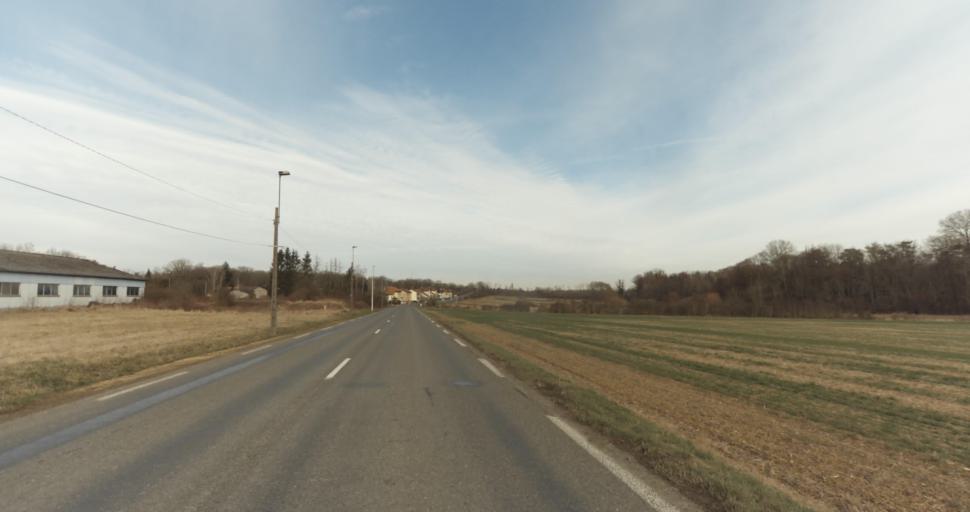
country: FR
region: Lorraine
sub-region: Departement de Meurthe-et-Moselle
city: Jarny
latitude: 49.1423
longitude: 5.8884
